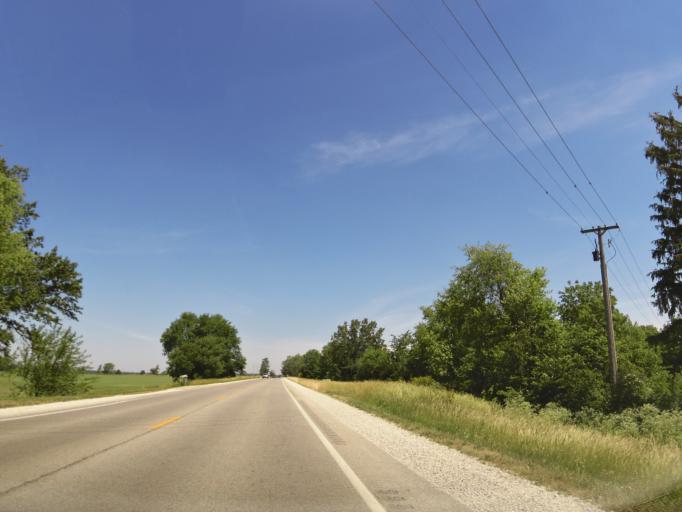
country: US
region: Illinois
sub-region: Vermilion County
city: Rossville
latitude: 40.3359
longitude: -87.6625
